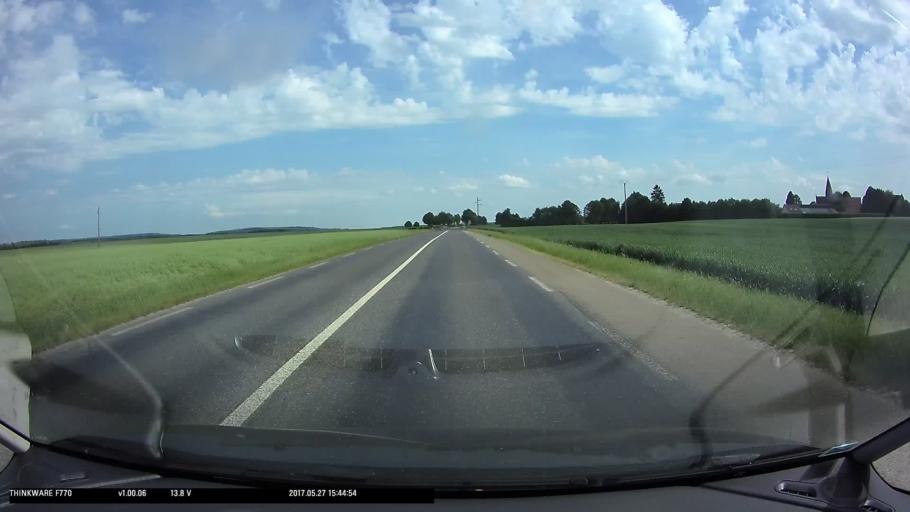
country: FR
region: Ile-de-France
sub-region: Departement du Val-d'Oise
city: Chars
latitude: 49.1928
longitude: 1.8825
